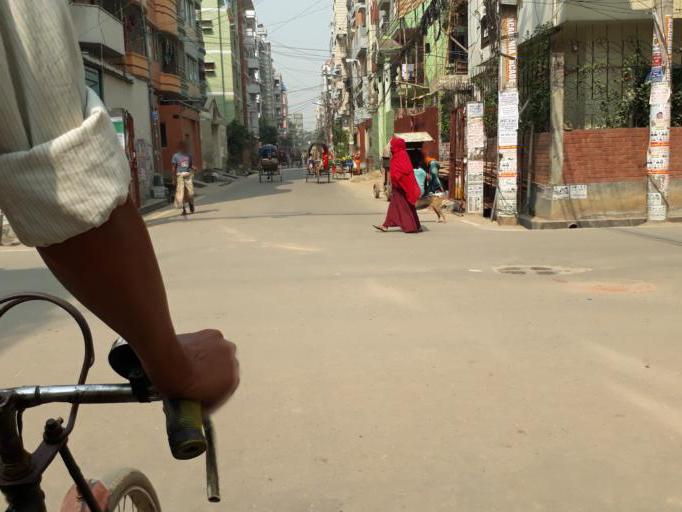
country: BD
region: Dhaka
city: Tungi
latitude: 23.8768
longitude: 90.3875
